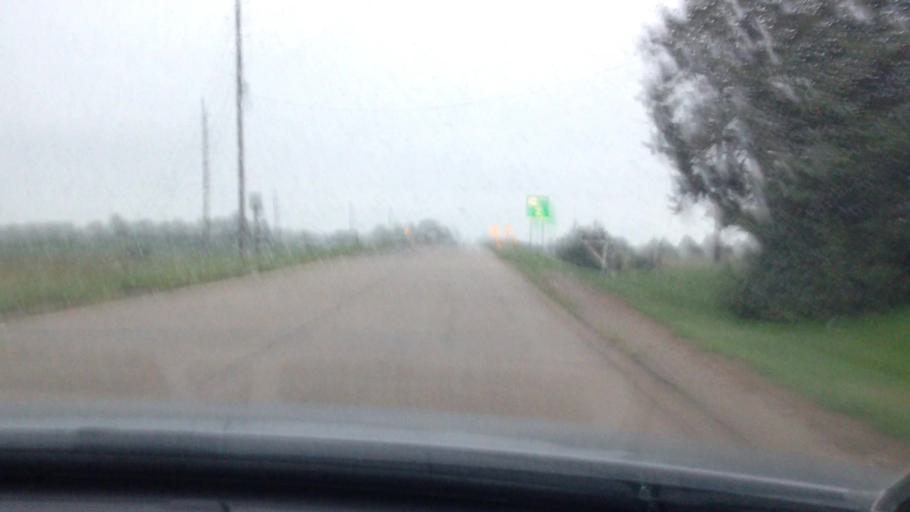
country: US
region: Kansas
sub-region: Brown County
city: Hiawatha
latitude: 39.8423
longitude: -95.5459
